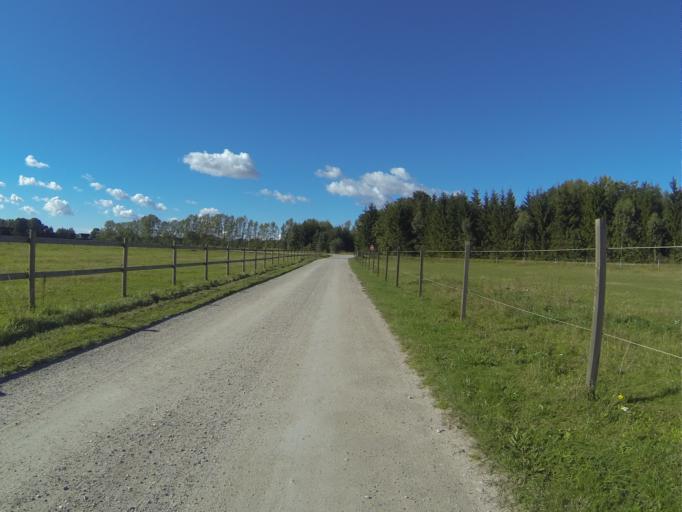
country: SE
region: Skane
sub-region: Hoors Kommun
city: Loberod
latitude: 55.7316
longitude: 13.3878
